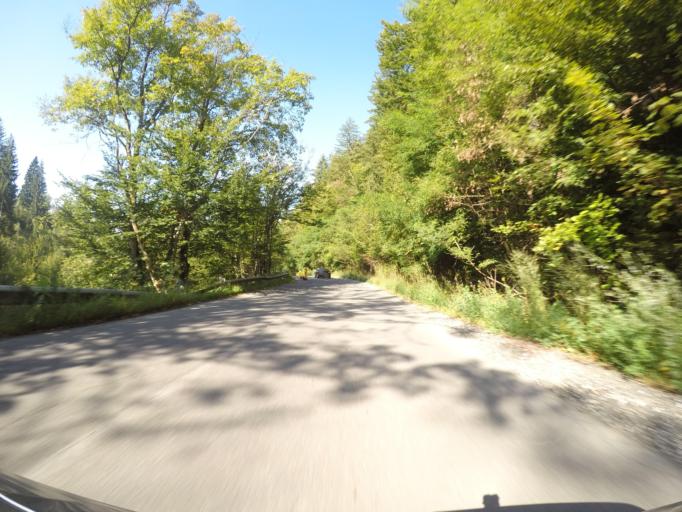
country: RO
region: Brasov
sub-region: Comuna Cristian
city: Cristian
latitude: 45.5938
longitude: 25.5334
